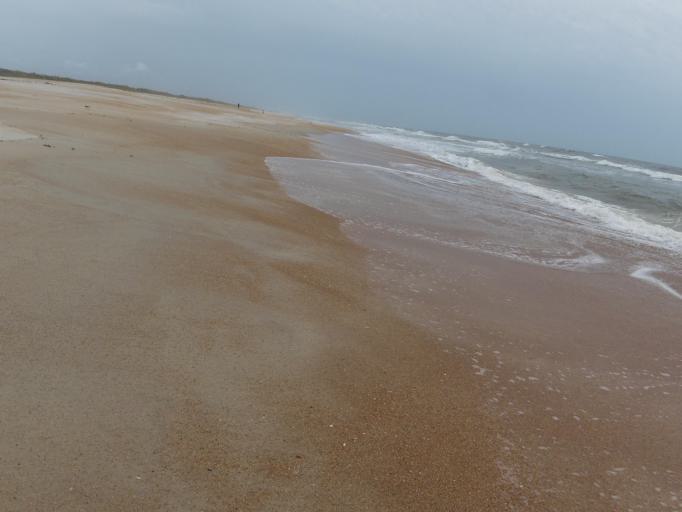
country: US
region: Florida
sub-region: Saint Johns County
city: Saint Augustine Beach
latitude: 29.8750
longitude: -81.2698
